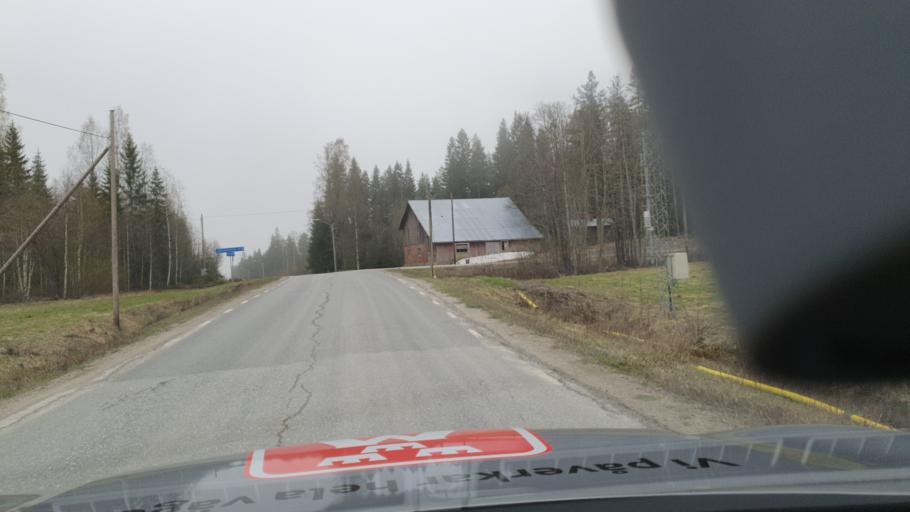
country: SE
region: Vaesternorrland
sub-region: OErnskoeldsviks Kommun
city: Husum
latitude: 63.5908
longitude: 19.0168
